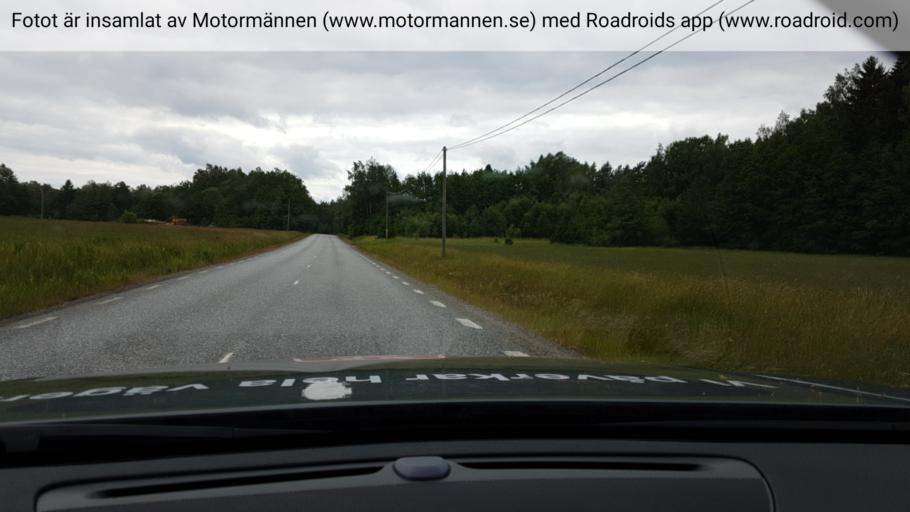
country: SE
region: Stockholm
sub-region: Haninge Kommun
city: Jordbro
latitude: 58.9995
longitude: 18.1085
